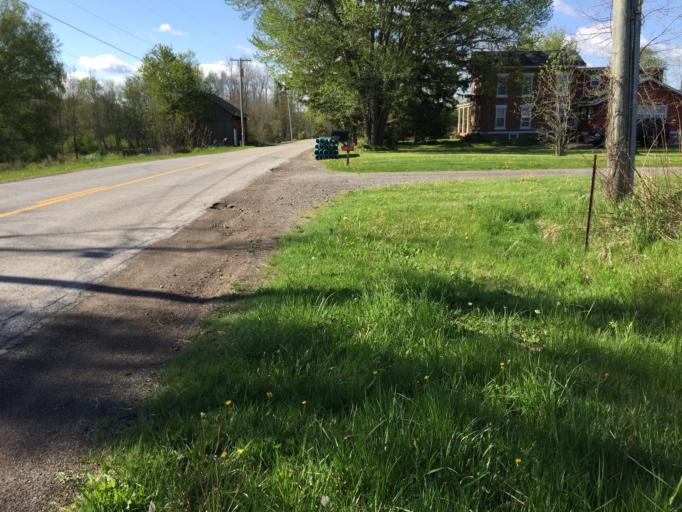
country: US
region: New York
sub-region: Wayne County
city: Marion
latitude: 43.1441
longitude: -77.1697
